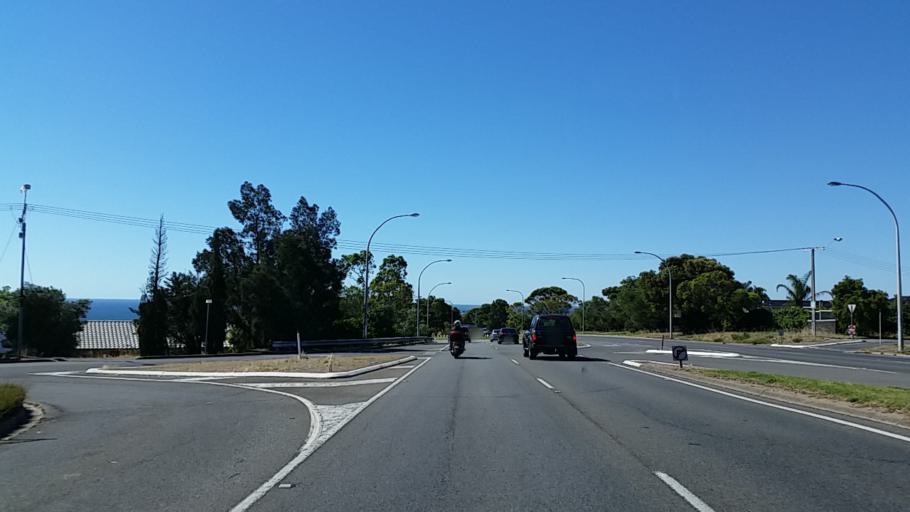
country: AU
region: South Australia
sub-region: Adelaide Hills
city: Seacliff
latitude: -35.0429
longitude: 138.5305
